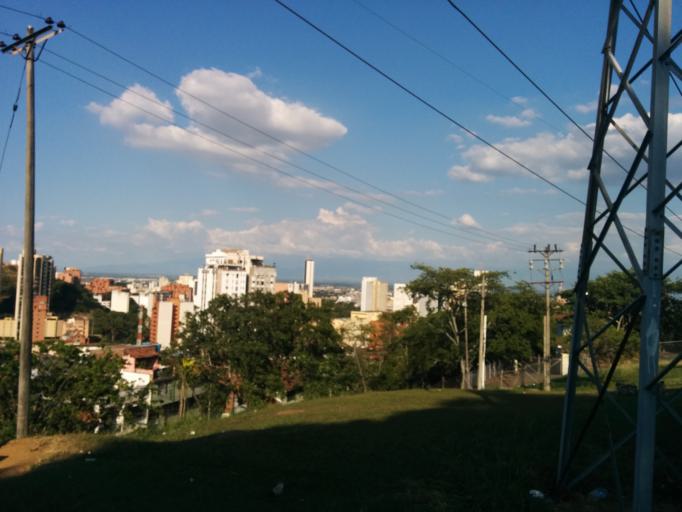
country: CO
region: Valle del Cauca
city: Cali
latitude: 3.4476
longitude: -76.5433
